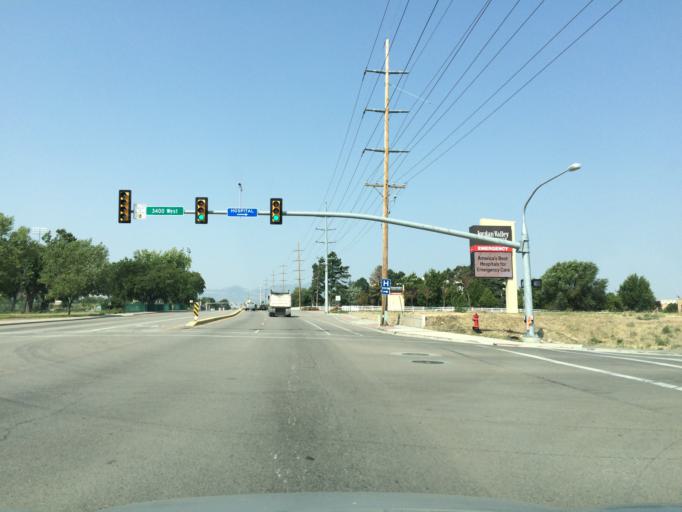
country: US
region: Utah
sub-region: Salt Lake County
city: South Jordan Heights
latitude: 40.5879
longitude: -111.9719
